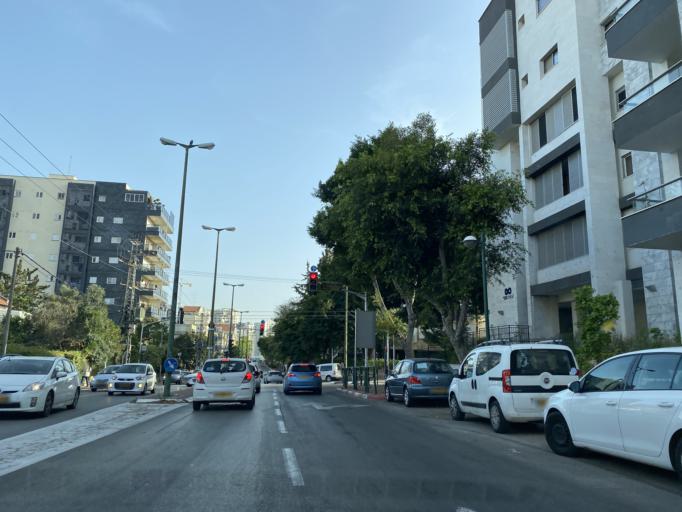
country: IL
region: Central District
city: Kfar Saba
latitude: 32.1750
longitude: 34.9022
